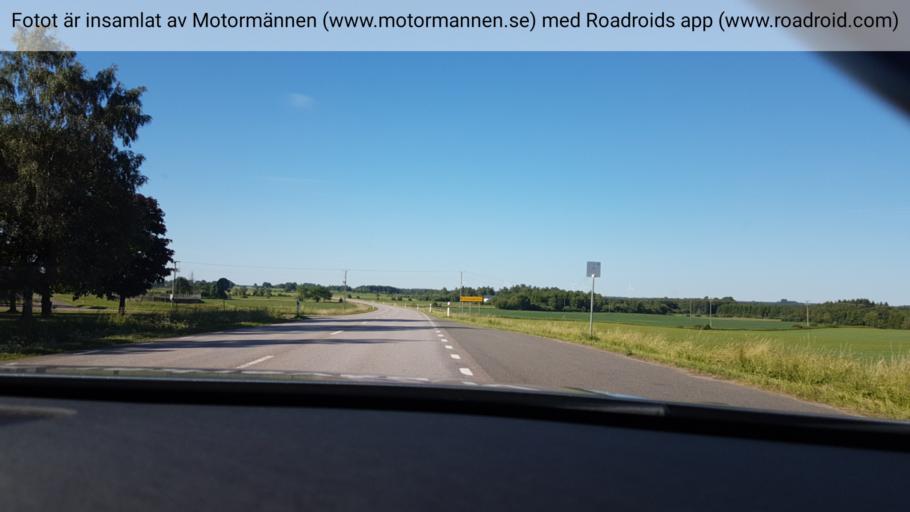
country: SE
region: Vaestra Goetaland
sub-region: Falkopings Kommun
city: Falkoeping
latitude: 58.1246
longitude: 13.5507
